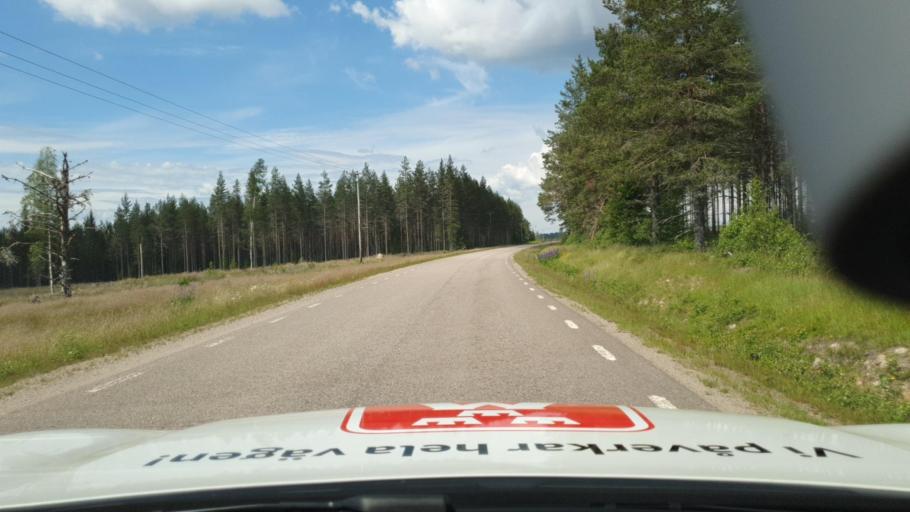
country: SE
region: Vaermland
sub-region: Torsby Kommun
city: Torsby
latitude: 60.4997
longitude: 12.8577
